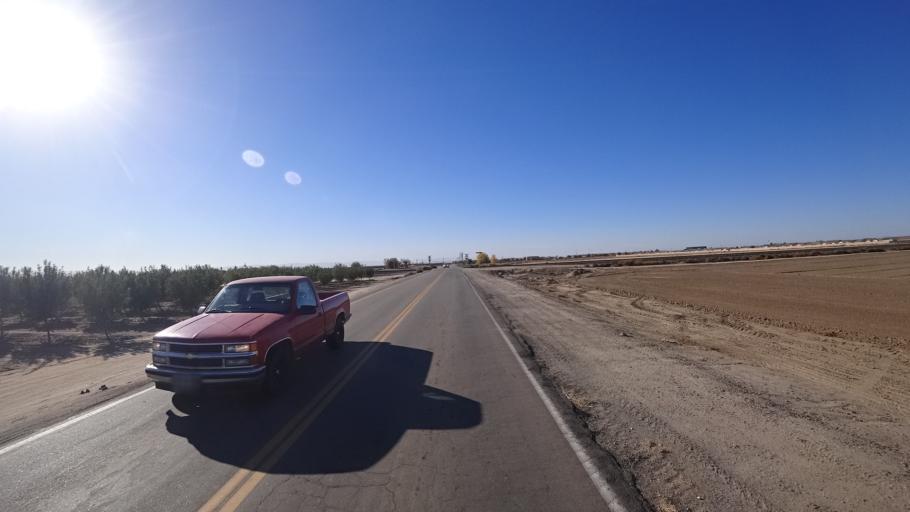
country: US
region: California
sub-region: Kern County
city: Greenfield
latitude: 35.2817
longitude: -119.1001
